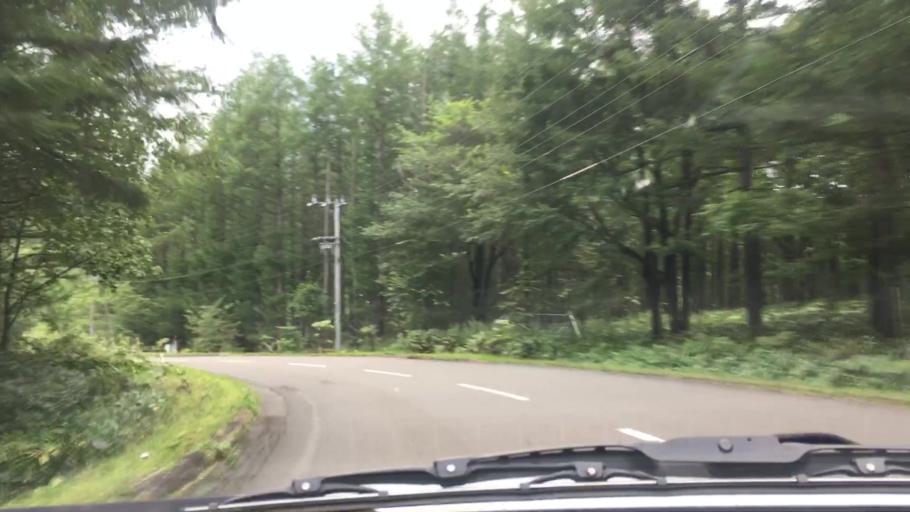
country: JP
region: Hokkaido
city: Otofuke
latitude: 43.1556
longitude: 142.8575
